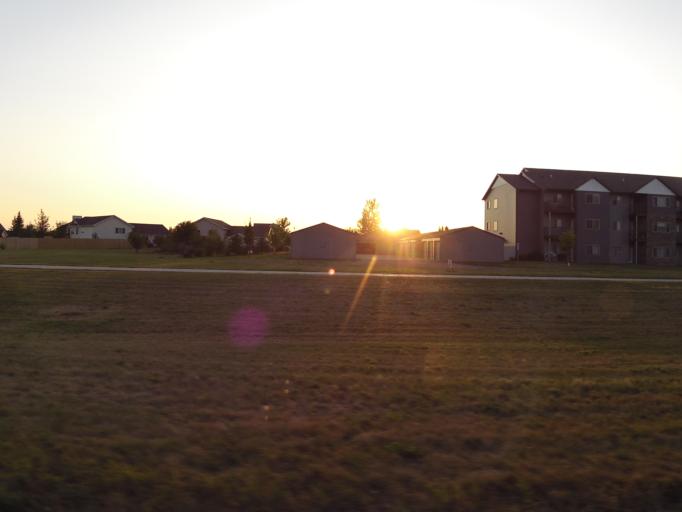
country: US
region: North Dakota
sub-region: Grand Forks County
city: Grand Forks
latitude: 47.8726
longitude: -97.0456
